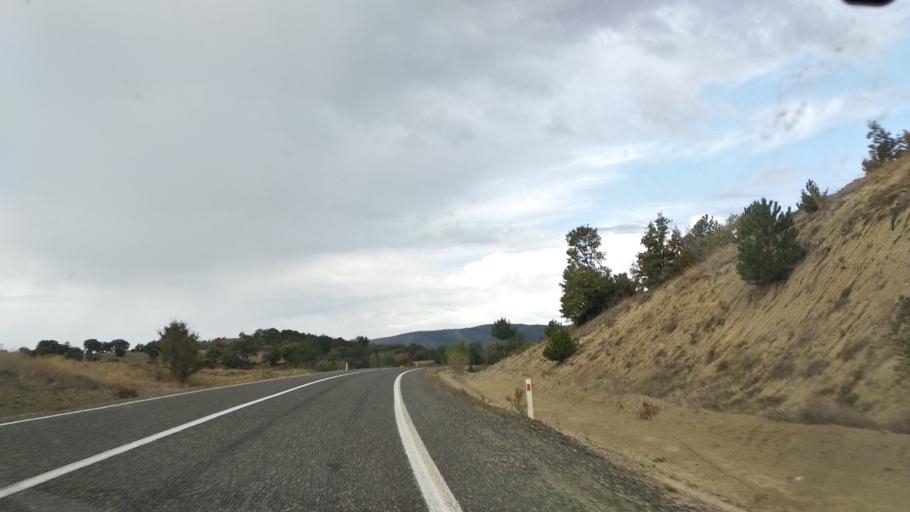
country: TR
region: Bolu
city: Seben
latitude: 40.3329
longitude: 31.4441
